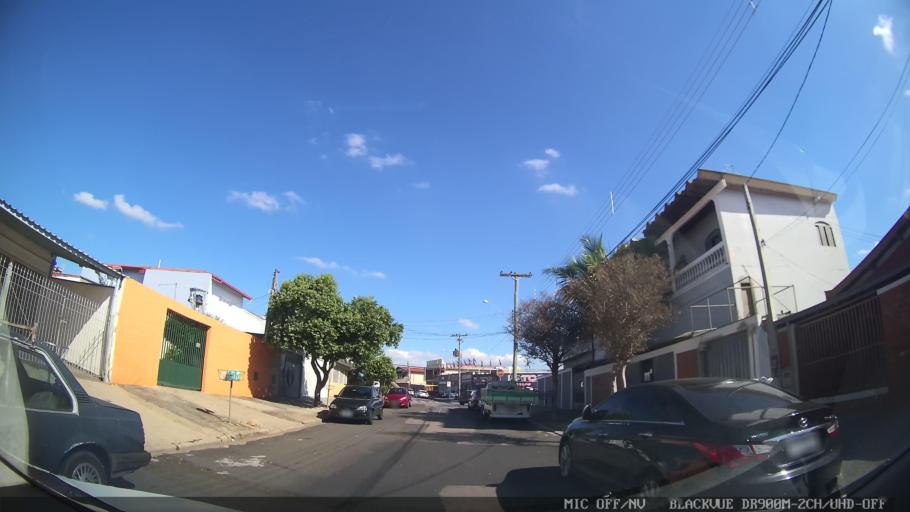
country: BR
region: Sao Paulo
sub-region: Campinas
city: Campinas
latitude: -22.9257
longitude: -47.1043
